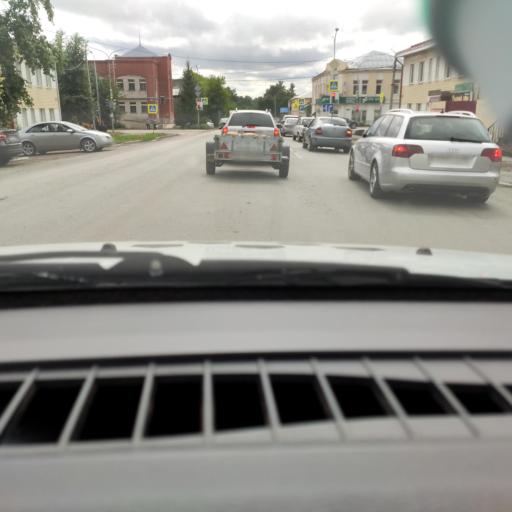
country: RU
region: Sverdlovsk
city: Krasnoufimsk
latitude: 56.6203
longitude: 57.7722
